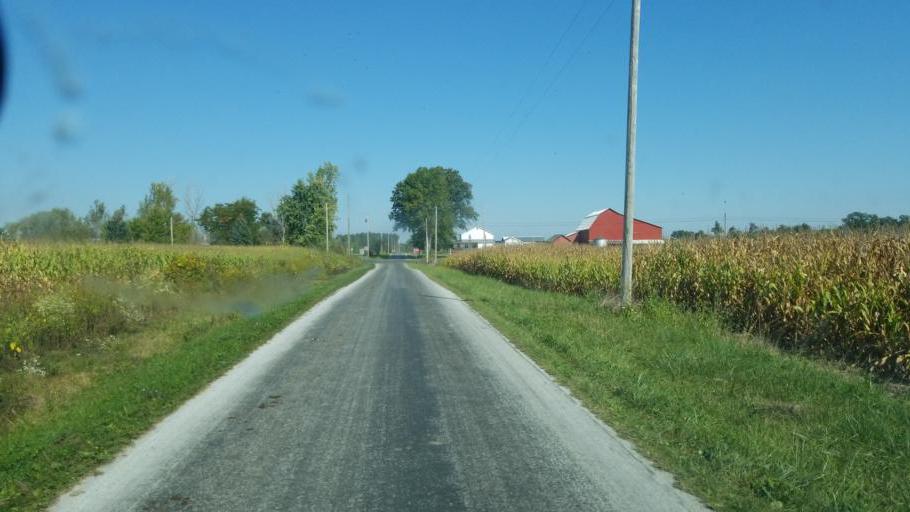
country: US
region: Ohio
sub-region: Hardin County
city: Kenton
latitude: 40.5658
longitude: -83.4872
